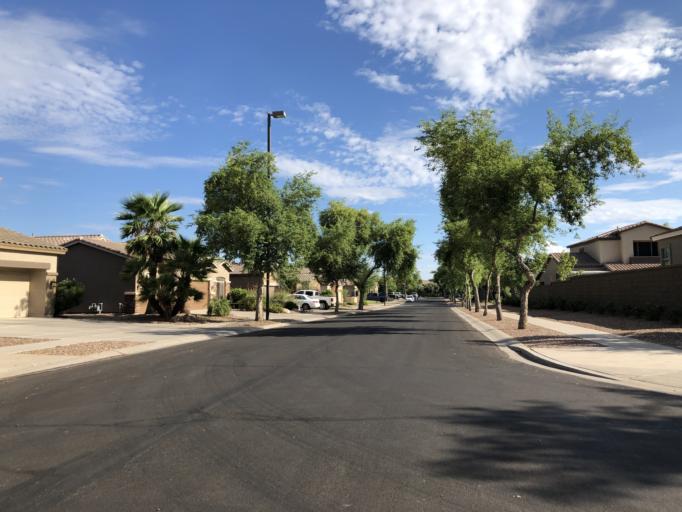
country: US
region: Arizona
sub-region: Maricopa County
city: Queen Creek
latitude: 33.2651
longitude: -111.7028
